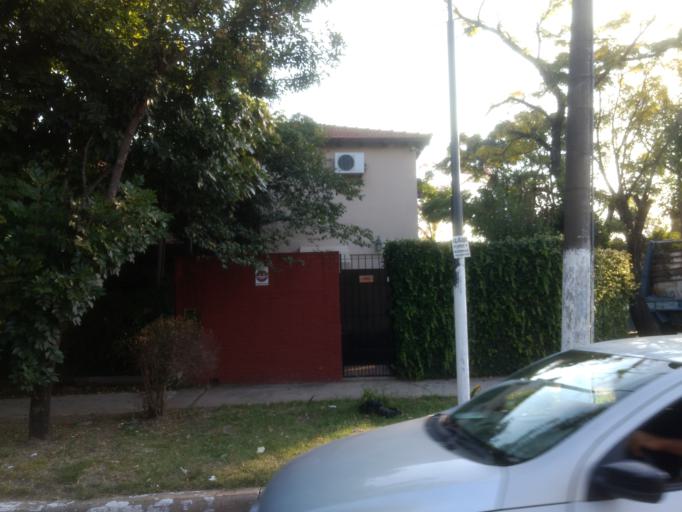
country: AR
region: Buenos Aires
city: Hurlingham
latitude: -34.5707
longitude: -58.6952
